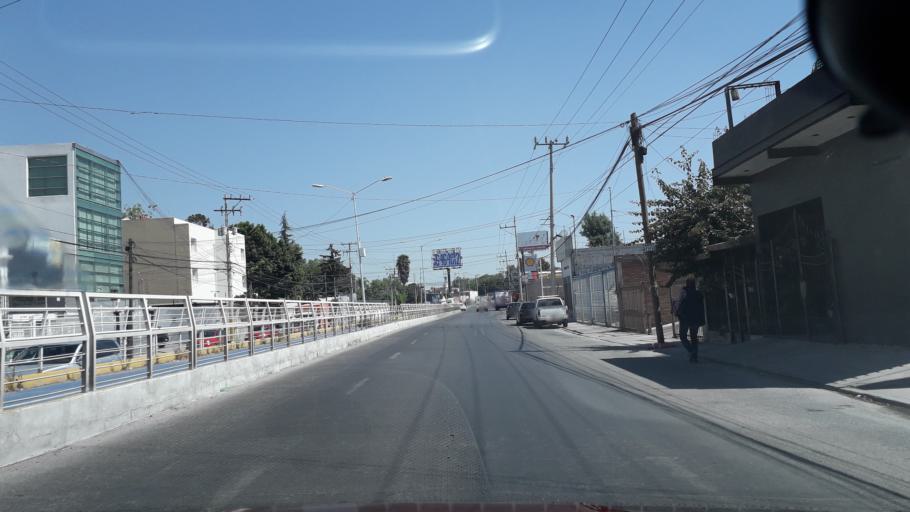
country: MX
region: Puebla
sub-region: Cuautlancingo
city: Sanctorum
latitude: 19.0845
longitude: -98.2385
